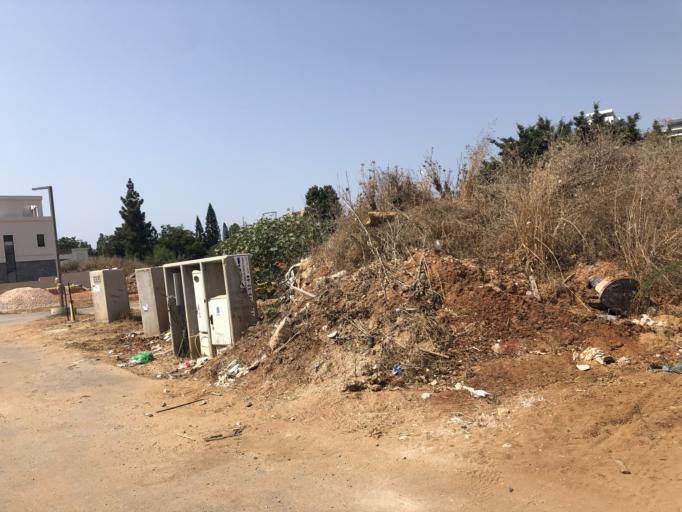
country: IL
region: Tel Aviv
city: Giv`atayim
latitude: 32.0561
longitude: 34.8305
